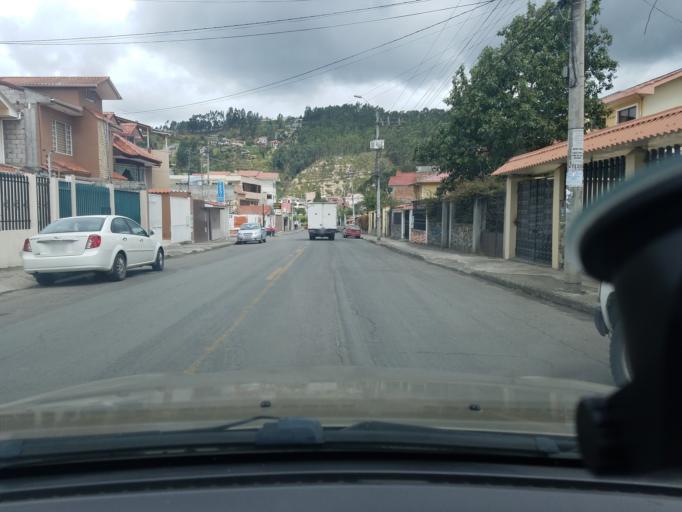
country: EC
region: Azuay
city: Cuenca
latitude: -2.9059
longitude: -78.9856
